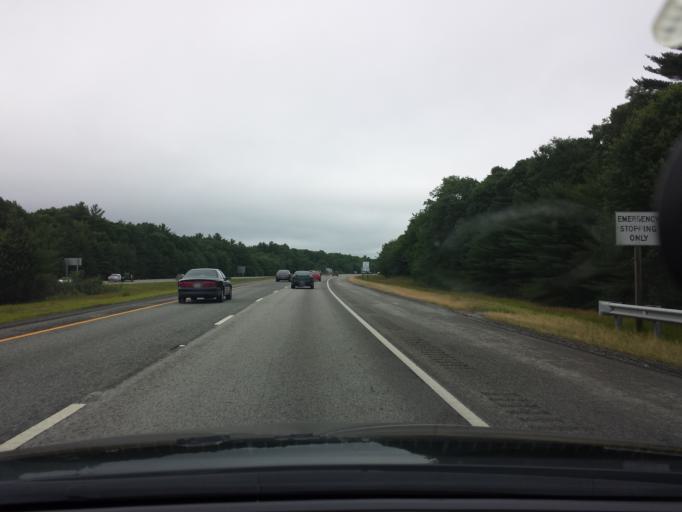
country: US
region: Rhode Island
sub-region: Kent County
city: West Greenwich
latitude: 41.6095
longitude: -71.6544
